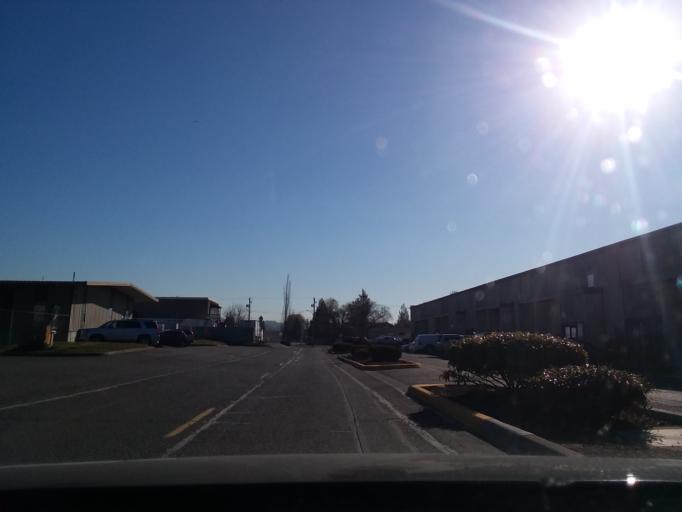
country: US
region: Washington
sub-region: Pierce County
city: Fife
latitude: 47.2443
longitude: -122.3693
